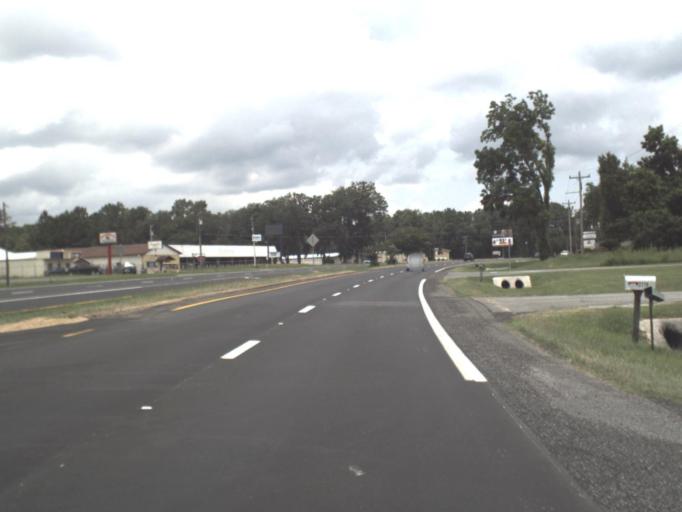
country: US
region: Florida
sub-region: Columbia County
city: Lake City
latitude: 30.1507
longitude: -82.6424
